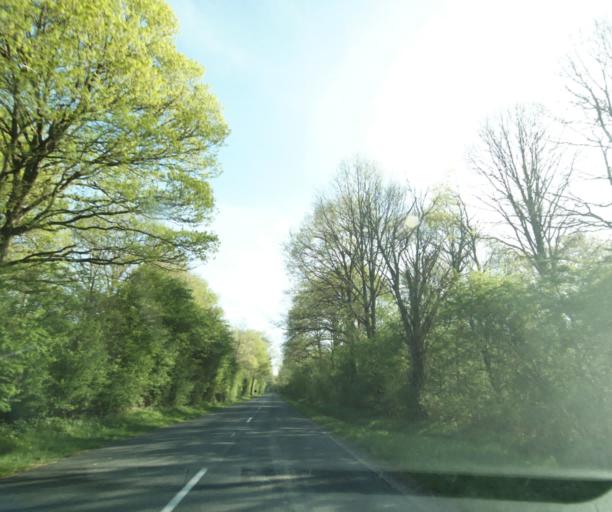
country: FR
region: Ile-de-France
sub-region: Departement de Seine-et-Marne
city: La Chapelle-Gauthier
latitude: 48.4885
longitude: 2.8854
